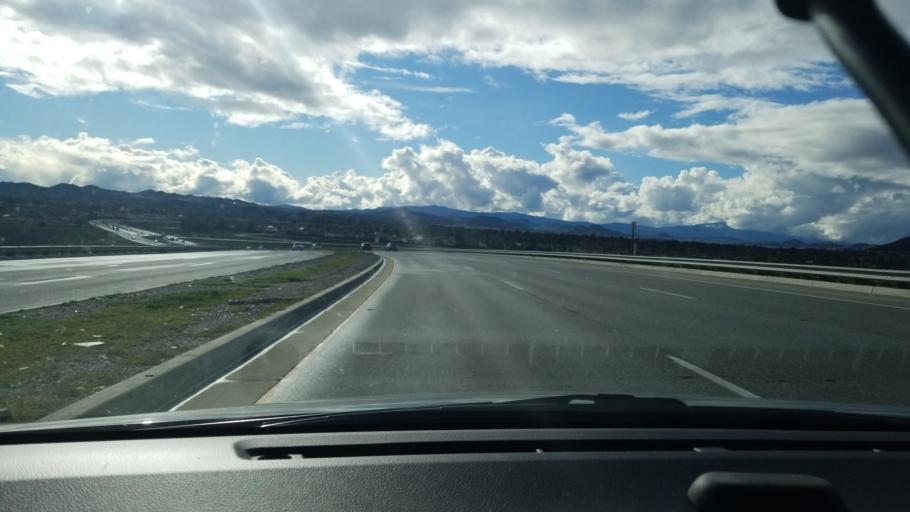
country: US
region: California
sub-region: Riverside County
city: Menifee
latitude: 33.6944
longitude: -117.1383
